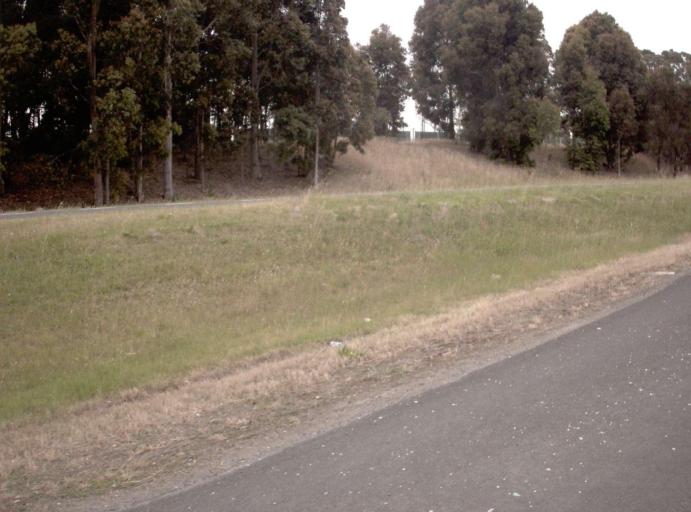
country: AU
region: Victoria
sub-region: Latrobe
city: Morwell
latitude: -38.2427
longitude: 146.4042
